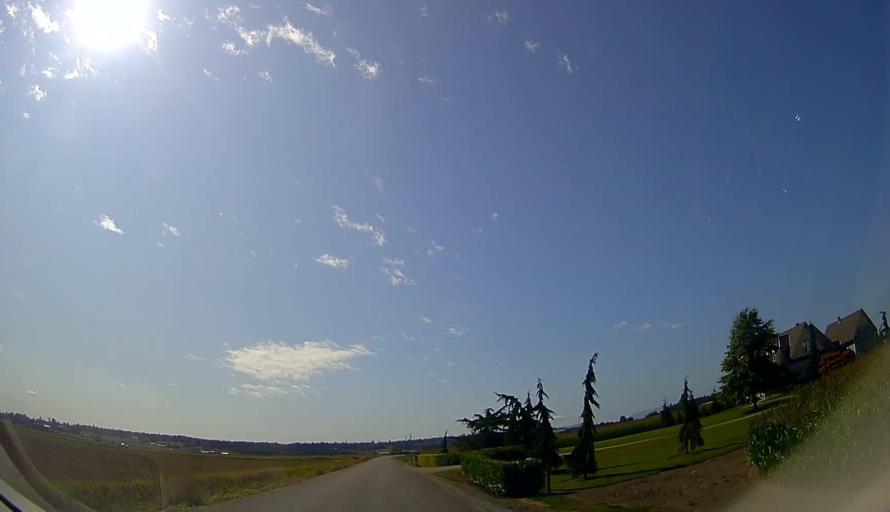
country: US
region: Washington
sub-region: Skagit County
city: Burlington
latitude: 48.4940
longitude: -122.3748
